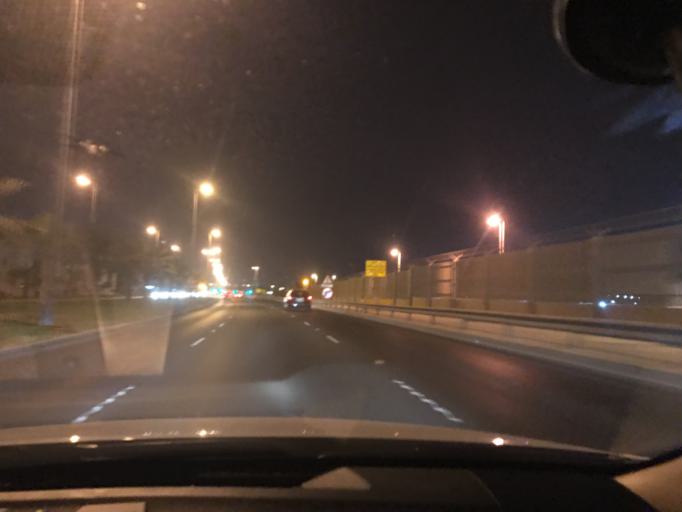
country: BH
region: Muharraq
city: Al Hadd
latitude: 26.2625
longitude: 50.6373
